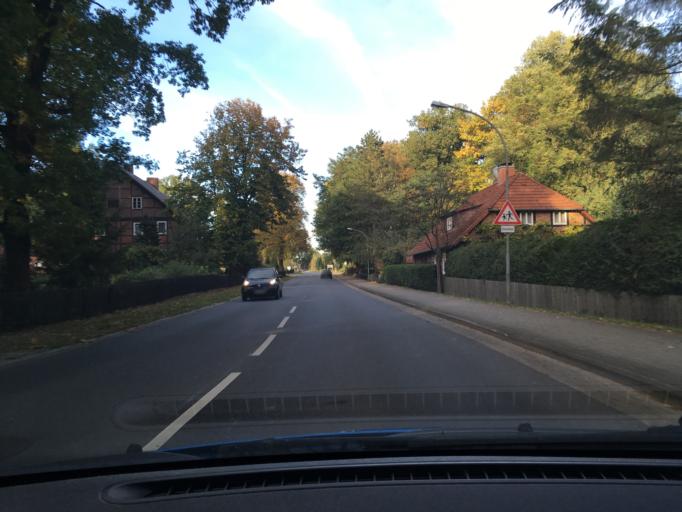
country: DE
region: Lower Saxony
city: Fassberg
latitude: 52.8984
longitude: 10.1257
